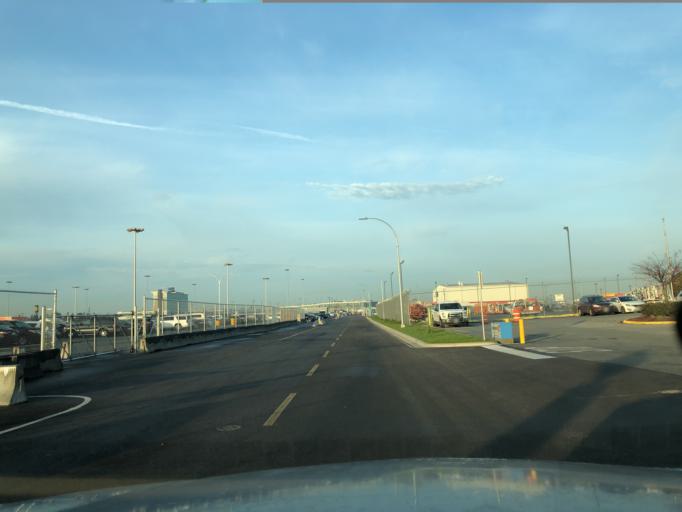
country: CA
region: British Columbia
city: Richmond
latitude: 49.1965
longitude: -123.1623
